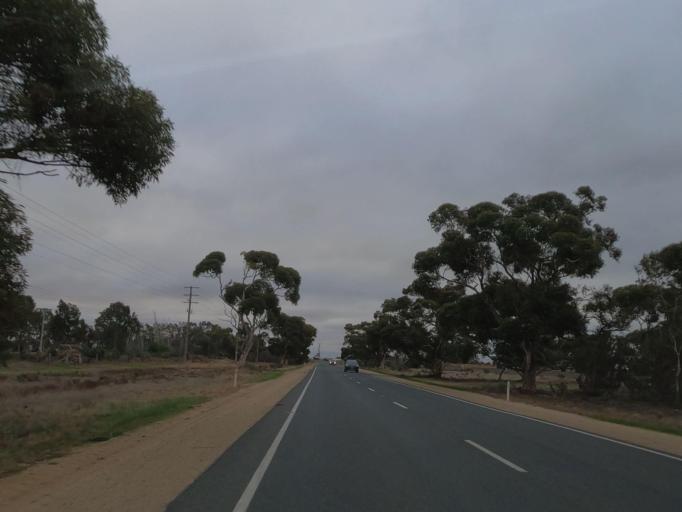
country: AU
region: Victoria
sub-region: Swan Hill
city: Swan Hill
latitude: -35.3980
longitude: 143.5748
